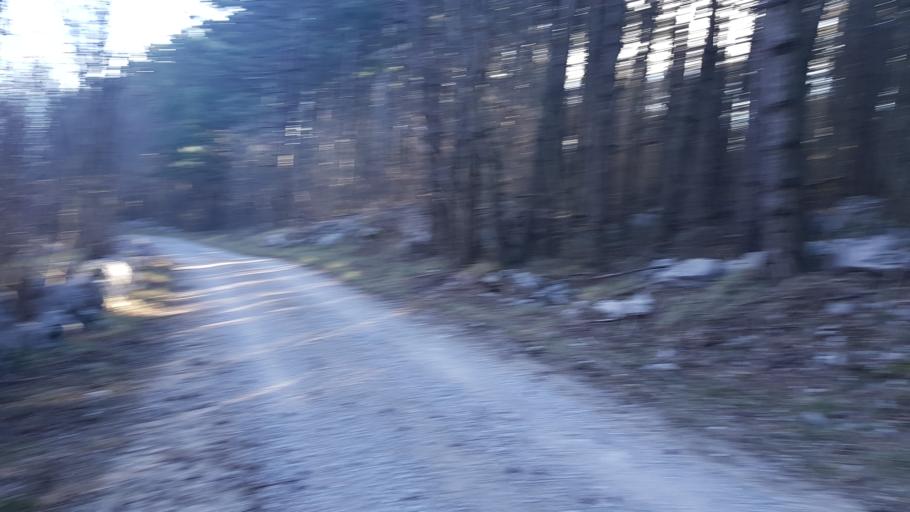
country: SI
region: Nova Gorica
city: Kromberk
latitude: 46.0183
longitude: 13.6998
